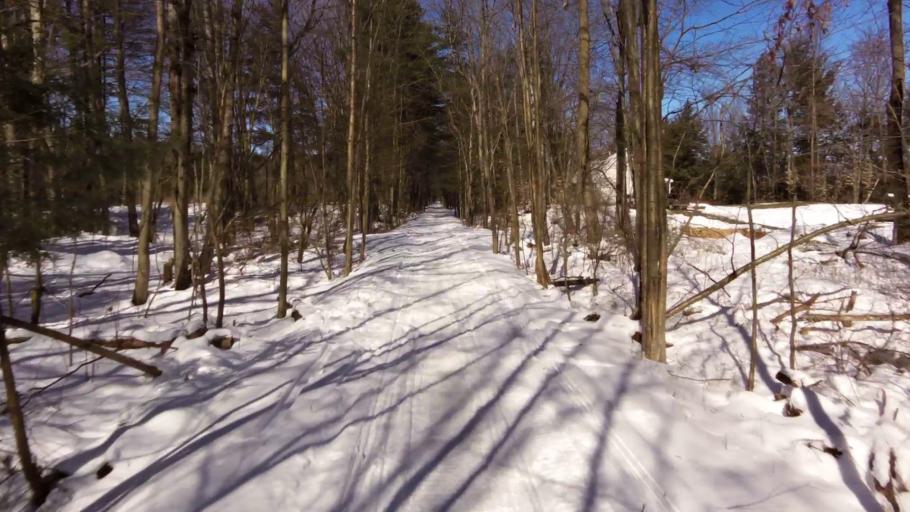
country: US
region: New York
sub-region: Allegany County
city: Houghton
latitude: 42.3566
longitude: -78.1286
